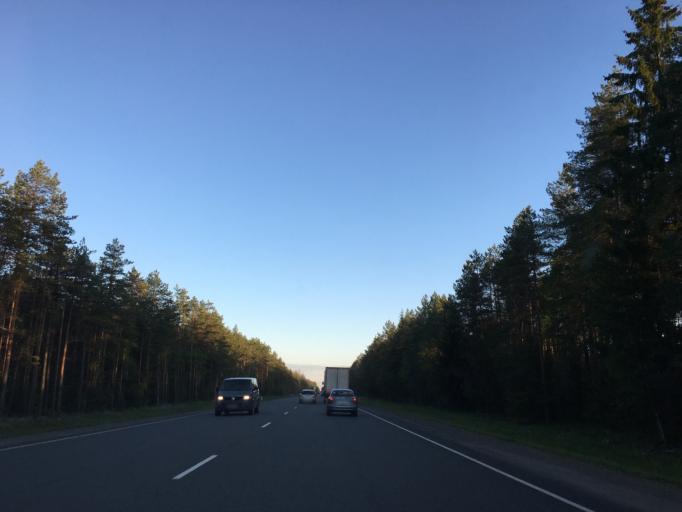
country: RU
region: Leningrad
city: Rozhdestveno
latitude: 59.2849
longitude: 29.9385
